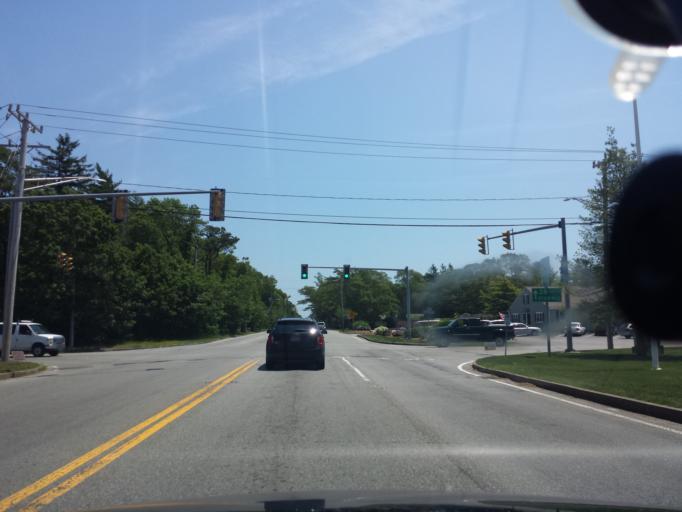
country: US
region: Massachusetts
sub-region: Barnstable County
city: Marstons Mills
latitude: 41.6534
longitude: -70.3927
